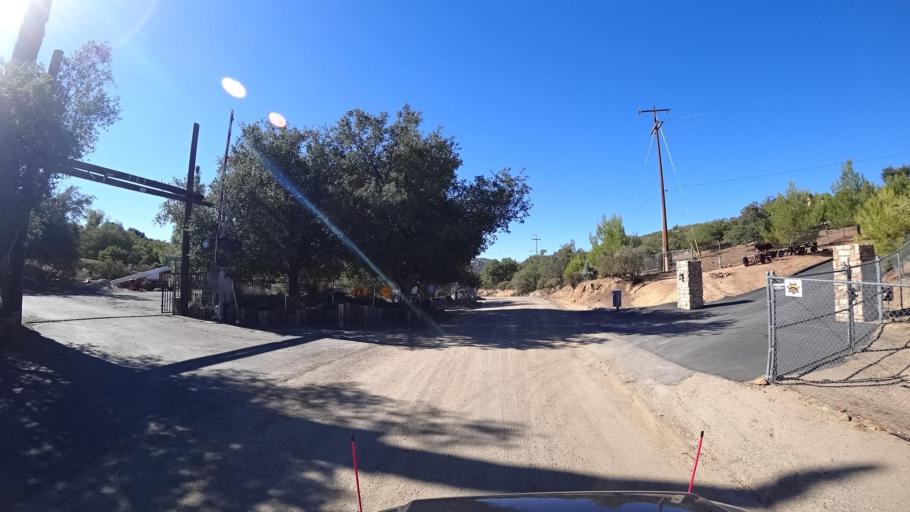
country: US
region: California
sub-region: San Diego County
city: Descanso
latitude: 32.8670
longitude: -116.6488
